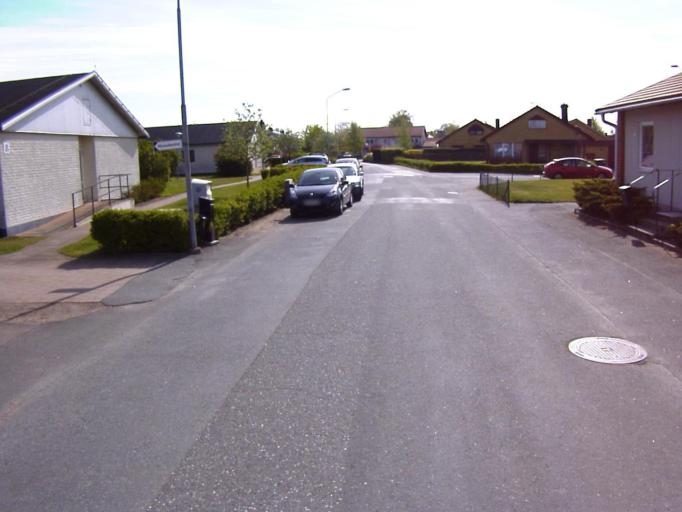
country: SE
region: Skane
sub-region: Kristianstads Kommun
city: Fjalkinge
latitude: 56.0428
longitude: 14.2730
